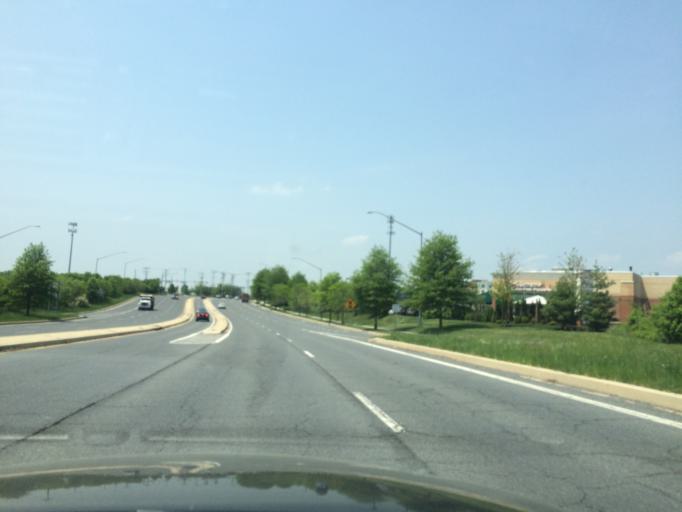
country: US
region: Maryland
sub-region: Howard County
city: Riverside
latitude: 39.1593
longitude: -76.8902
